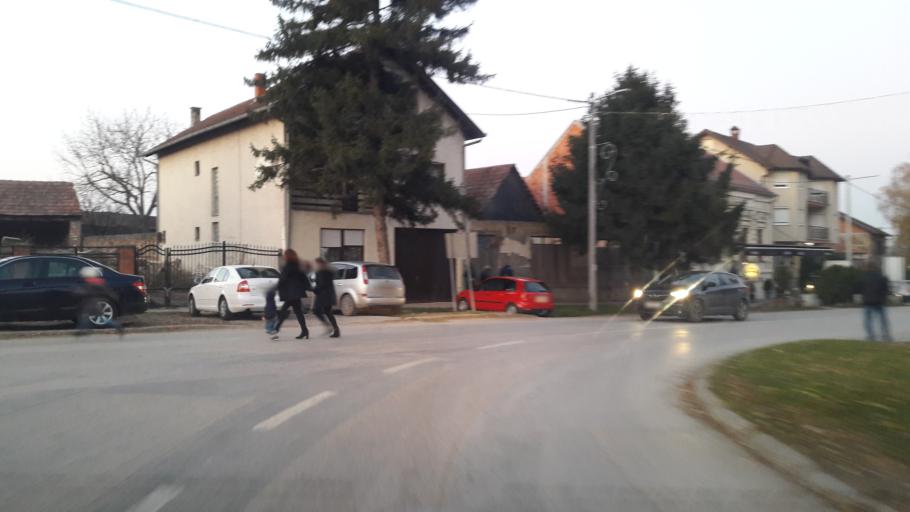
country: HR
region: Vukovarsko-Srijemska
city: Nijemci
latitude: 45.1401
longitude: 19.0354
